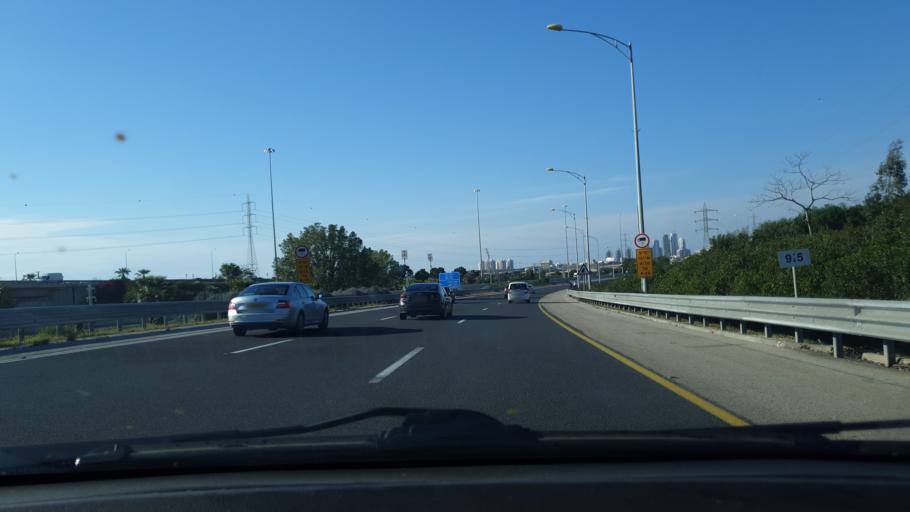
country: IL
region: Central District
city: Rishon LeZiyyon
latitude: 31.9696
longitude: 34.7580
